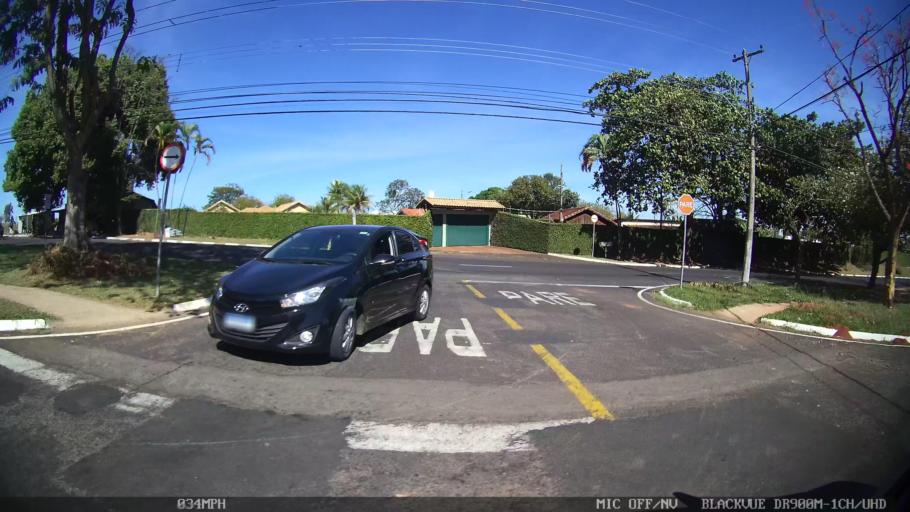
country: BR
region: Sao Paulo
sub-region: Franca
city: Franca
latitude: -20.5565
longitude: -47.3842
